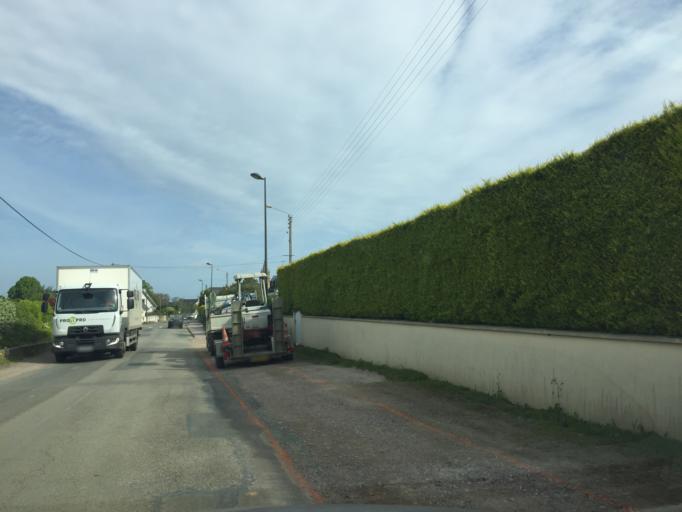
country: FR
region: Brittany
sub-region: Departement des Cotes-d'Armor
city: Matignon
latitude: 48.6517
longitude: -2.3309
